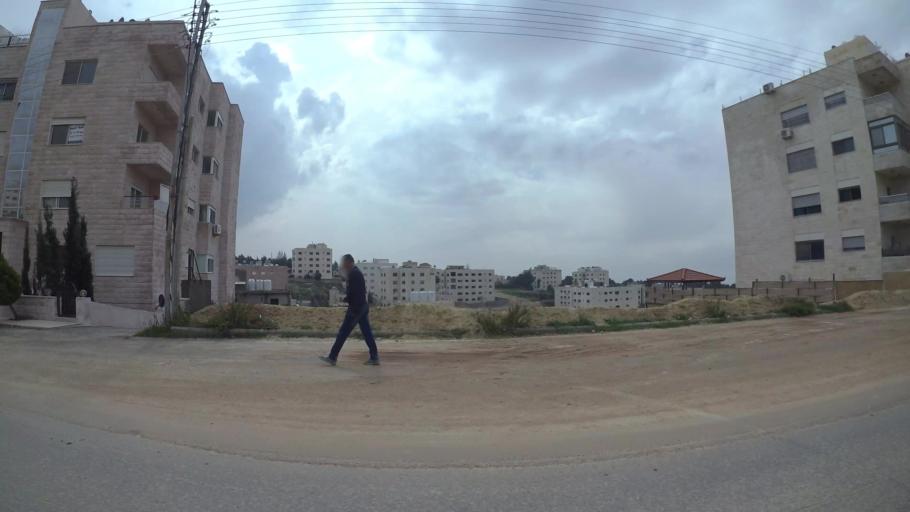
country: JO
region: Amman
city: Umm as Summaq
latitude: 31.9006
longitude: 35.8318
